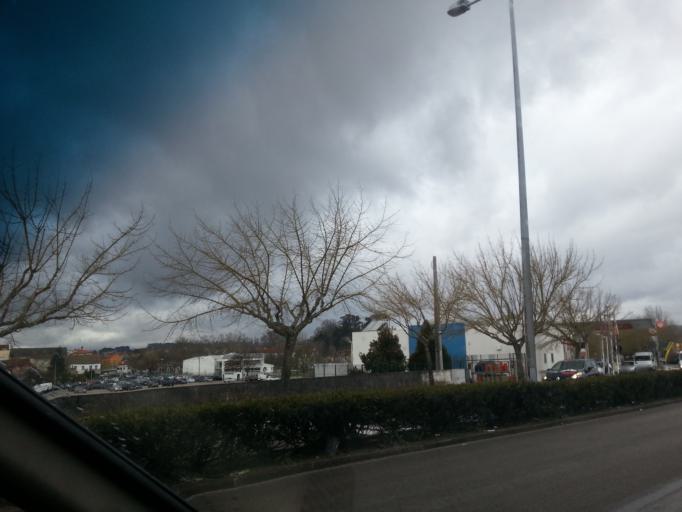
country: PT
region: Viseu
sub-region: Viseu
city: Viseu
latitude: 40.6627
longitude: -7.9052
